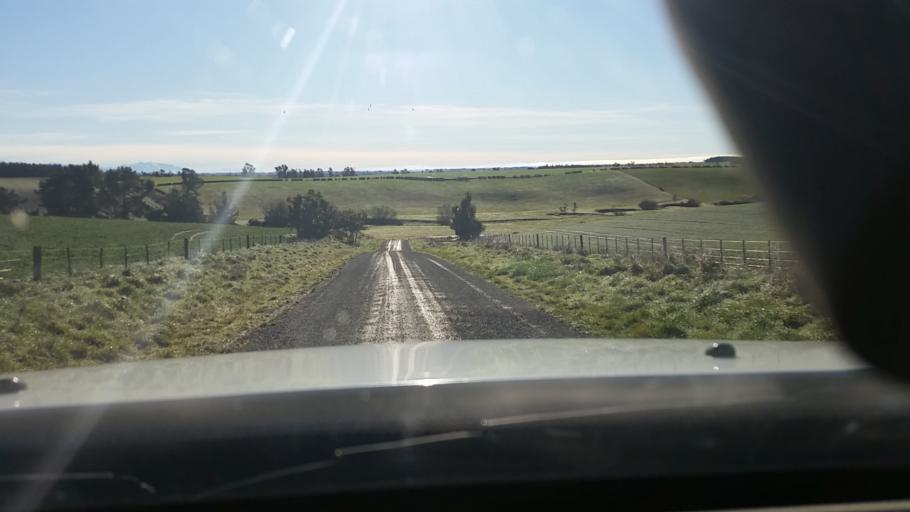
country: NZ
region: Canterbury
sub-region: Timaru District
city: Pleasant Point
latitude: -44.2044
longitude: 171.1850
